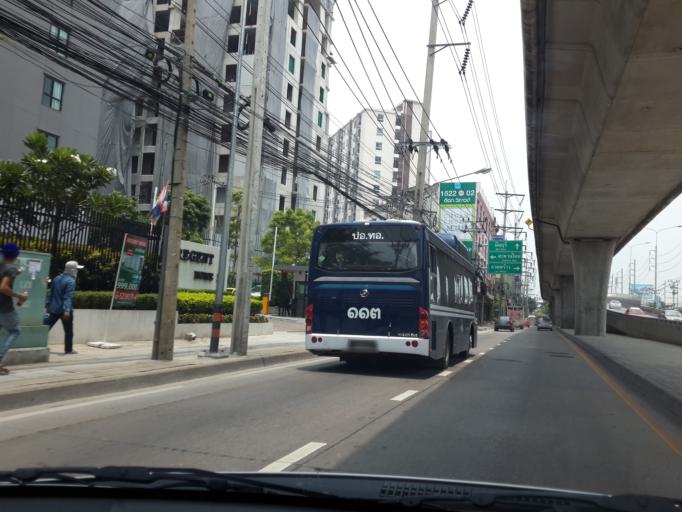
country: TH
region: Bangkok
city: Lak Si
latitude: 13.8773
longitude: 100.5940
